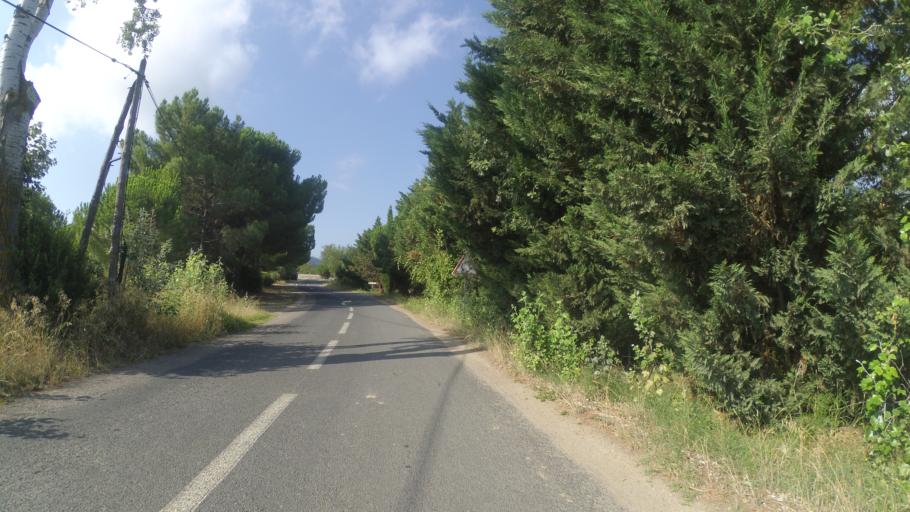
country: FR
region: Languedoc-Roussillon
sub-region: Departement des Pyrenees-Orientales
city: Millas
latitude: 42.6501
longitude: 2.7058
